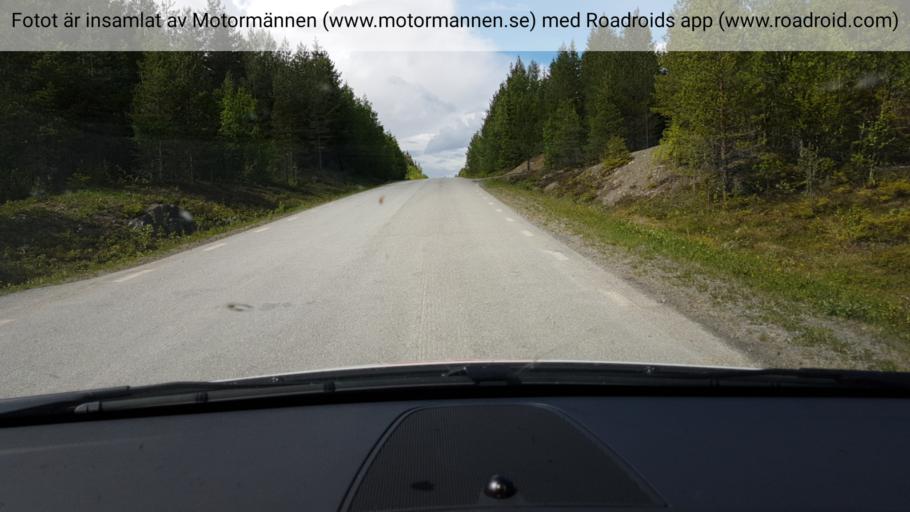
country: SE
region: Jaemtland
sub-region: Bergs Kommun
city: Hoverberg
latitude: 63.0279
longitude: 14.0655
